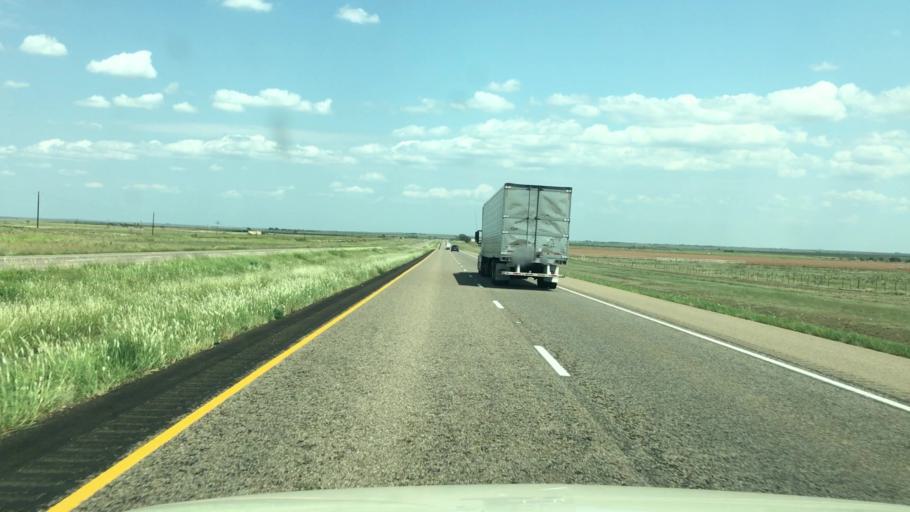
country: US
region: Texas
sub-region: Armstrong County
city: Claude
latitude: 35.0322
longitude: -101.1359
